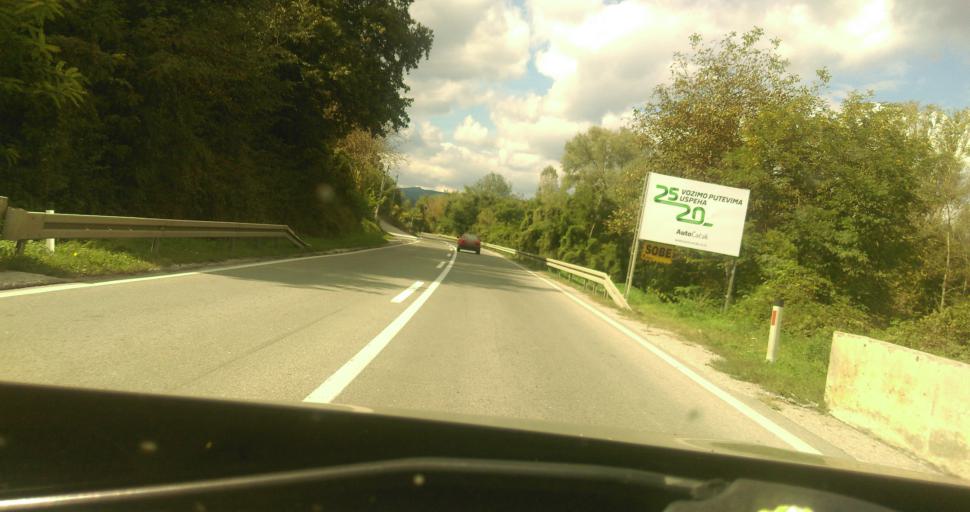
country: RS
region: Central Serbia
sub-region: Moravicki Okrug
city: Cacak
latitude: 43.8976
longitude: 20.2807
